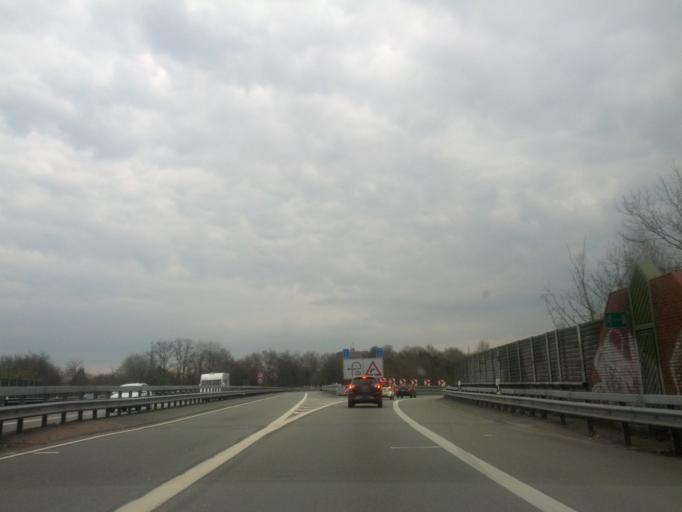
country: DE
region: Lower Saxony
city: Oldenburg
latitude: 53.1530
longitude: 8.1922
